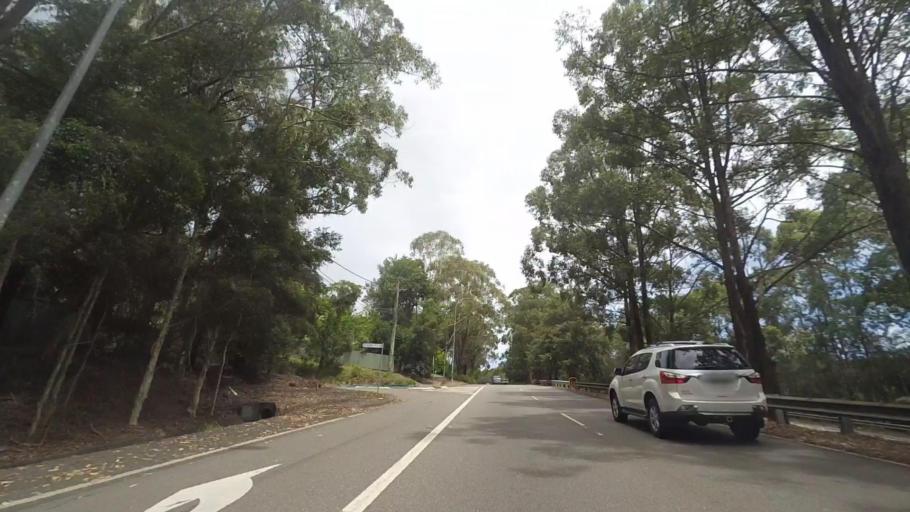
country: AU
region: New South Wales
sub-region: Wyong Shire
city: Berkeley Vale
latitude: -33.3481
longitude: 151.4312
